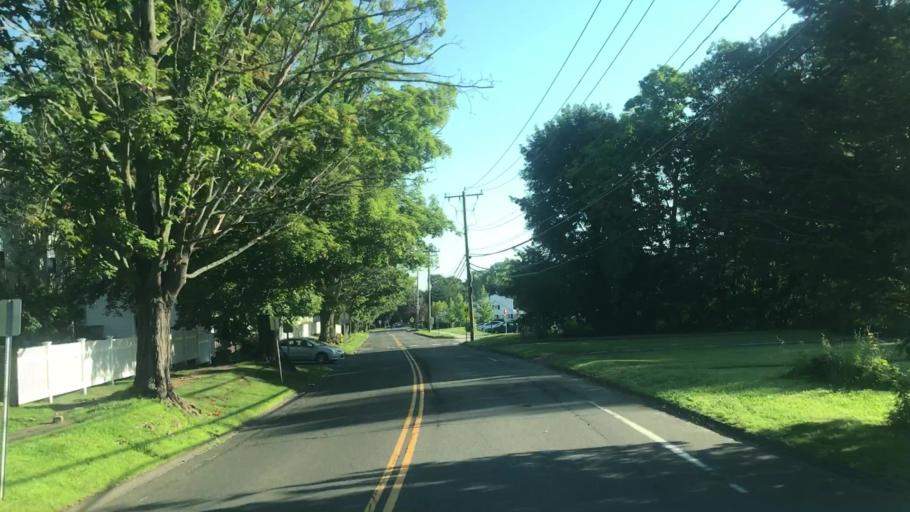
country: US
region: Connecticut
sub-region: Fairfield County
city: Danbury
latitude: 41.3846
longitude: -73.4633
